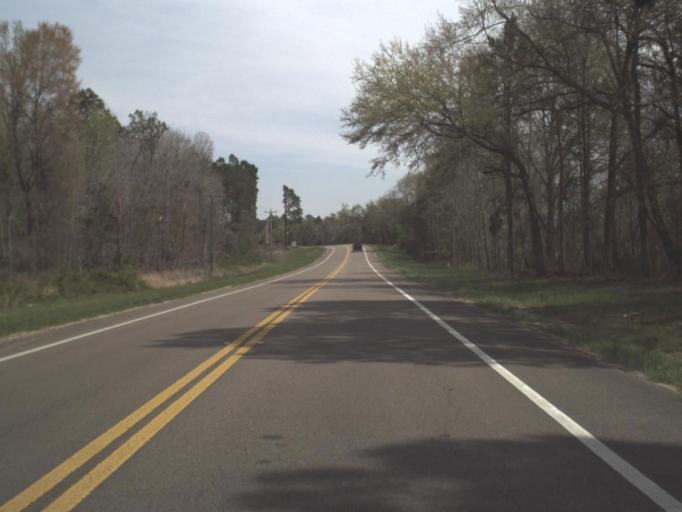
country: US
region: Alabama
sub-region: Geneva County
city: Geneva
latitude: 30.9501
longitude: -85.7364
